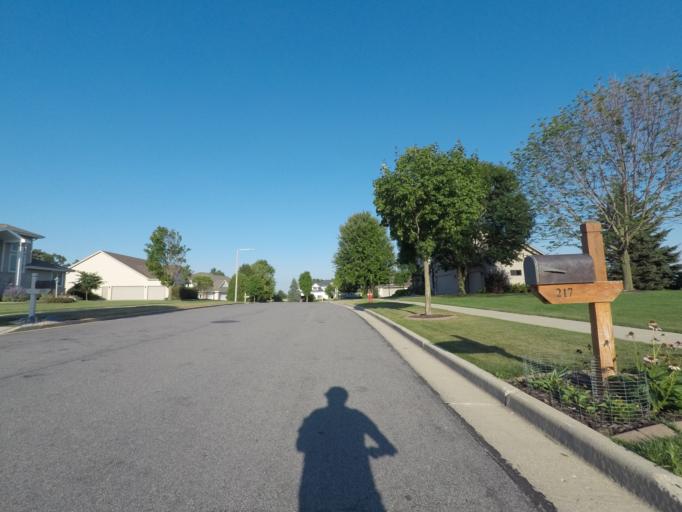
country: US
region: Wisconsin
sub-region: Dane County
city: Verona
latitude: 43.0066
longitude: -89.5362
